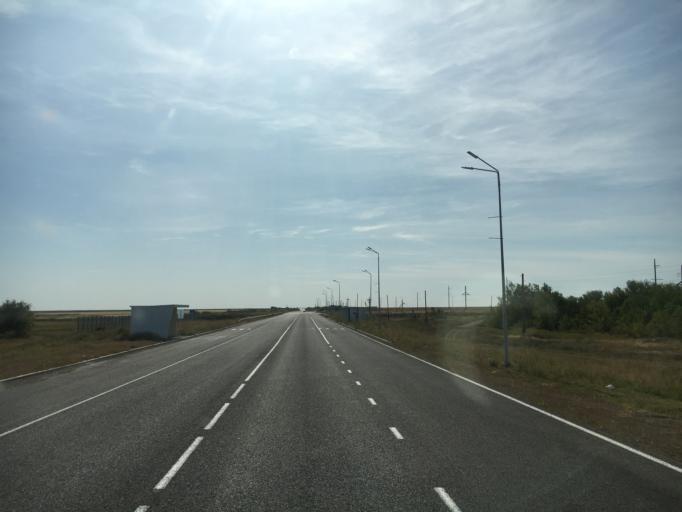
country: KZ
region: Batys Qazaqstan
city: Peremetnoe
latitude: 51.1355
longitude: 50.9081
